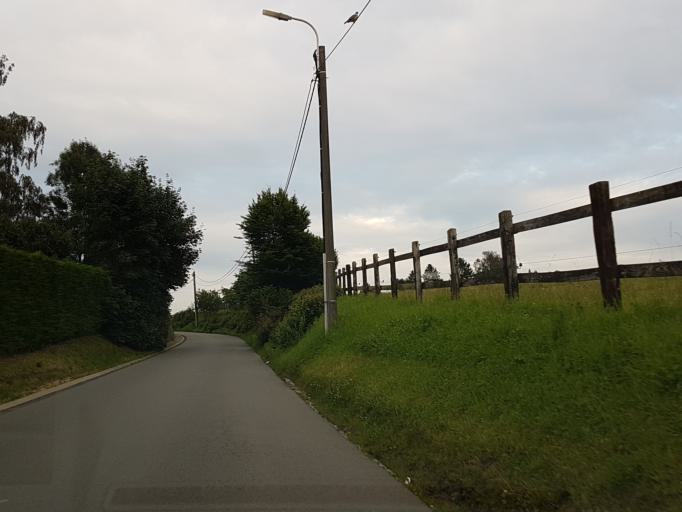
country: BE
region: Flanders
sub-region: Provincie Vlaams-Brabant
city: Ternat
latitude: 50.9011
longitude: 4.1649
